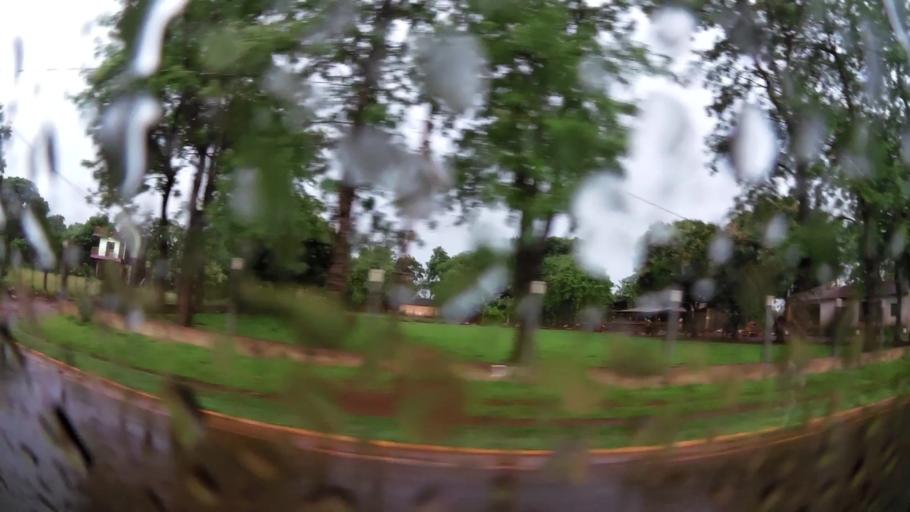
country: PY
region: Alto Parana
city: Presidente Franco
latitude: -25.5408
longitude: -54.6783
